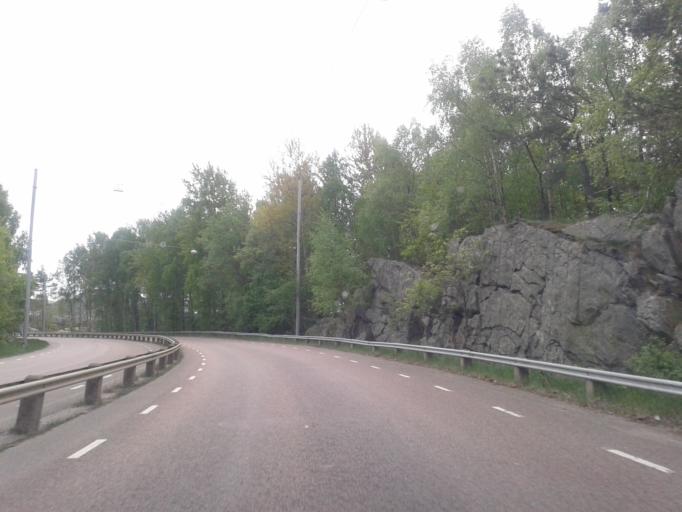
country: SE
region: Vaestra Goetaland
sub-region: Goteborg
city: Gardsten
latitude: 57.7992
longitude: 12.0236
